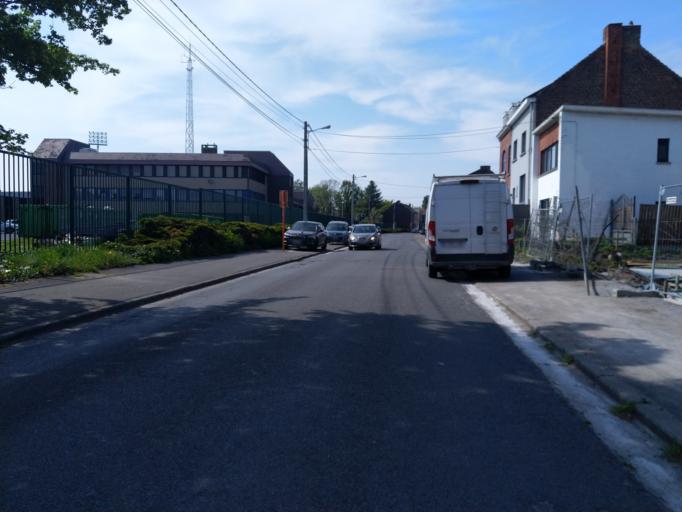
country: BE
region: Wallonia
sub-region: Province du Hainaut
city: Mons
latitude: 50.4621
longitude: 3.9676
